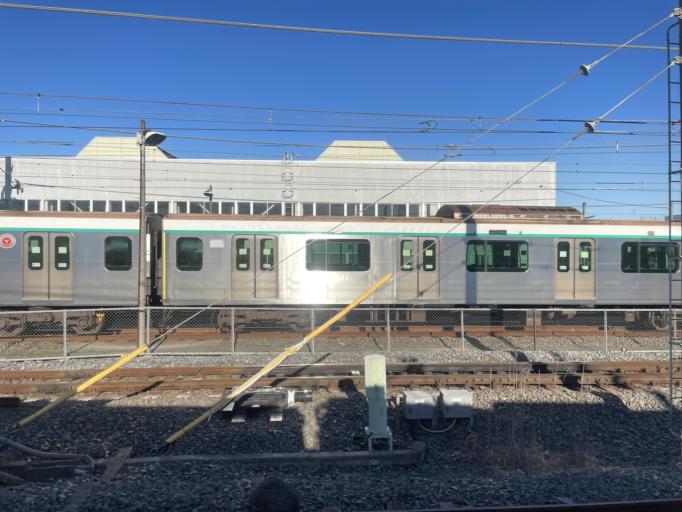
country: JP
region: Saitama
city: Kurihashi
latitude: 36.1177
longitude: 139.7076
